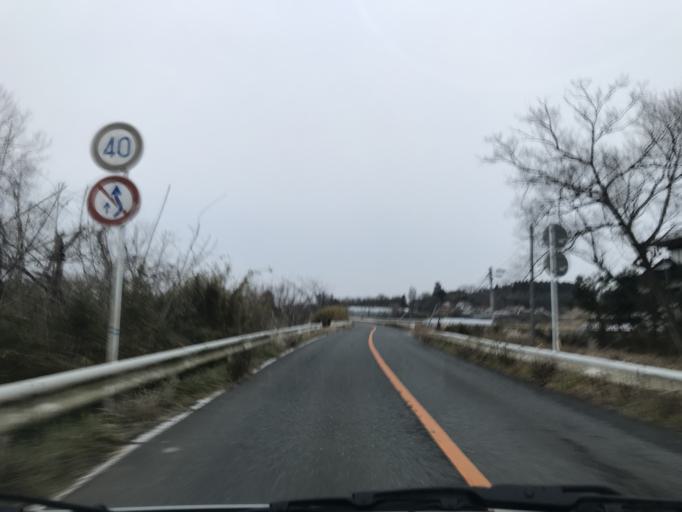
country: JP
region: Miyagi
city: Kogota
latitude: 38.7062
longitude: 141.0995
